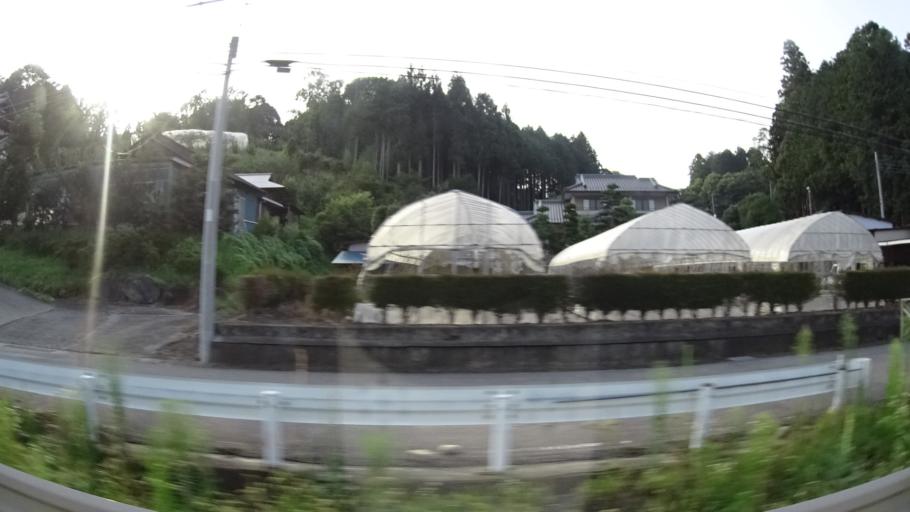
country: JP
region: Tochigi
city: Karasuyama
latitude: 36.5909
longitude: 140.1190
